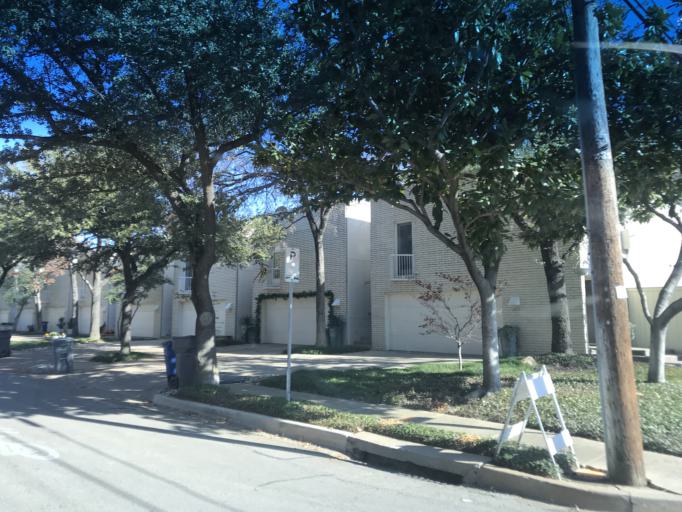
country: US
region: Texas
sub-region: Dallas County
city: Dallas
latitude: 32.8063
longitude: -96.8102
